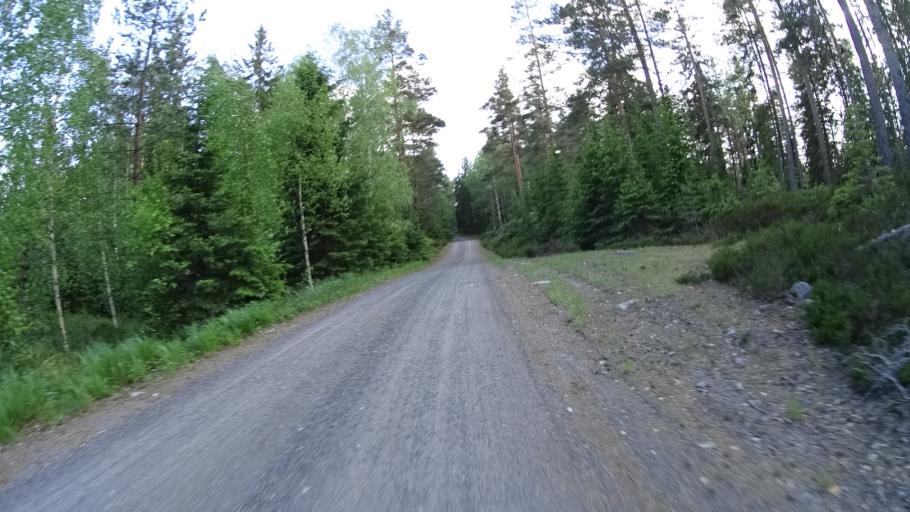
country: FI
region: Uusimaa
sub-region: Raaseporin
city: Pohja
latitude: 60.1601
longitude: 23.4915
